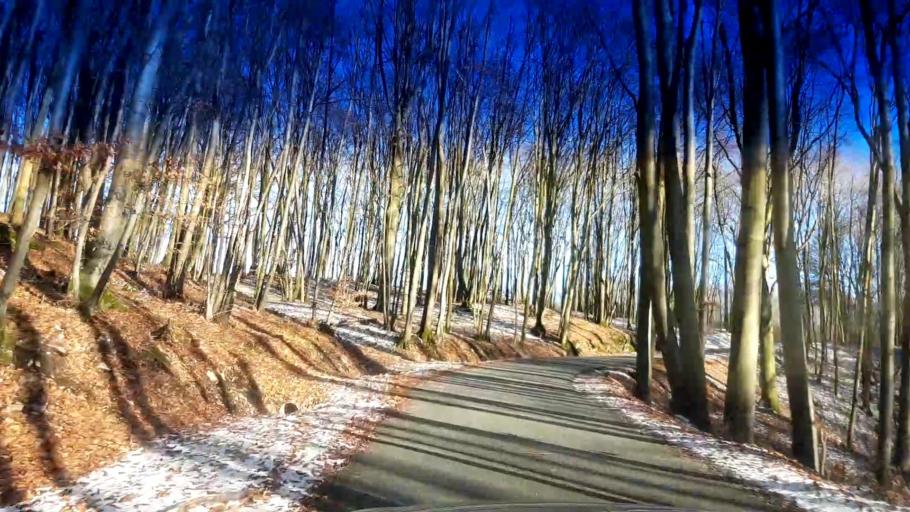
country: DE
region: Bavaria
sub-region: Upper Franconia
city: Buttenheim
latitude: 49.8352
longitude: 11.0842
